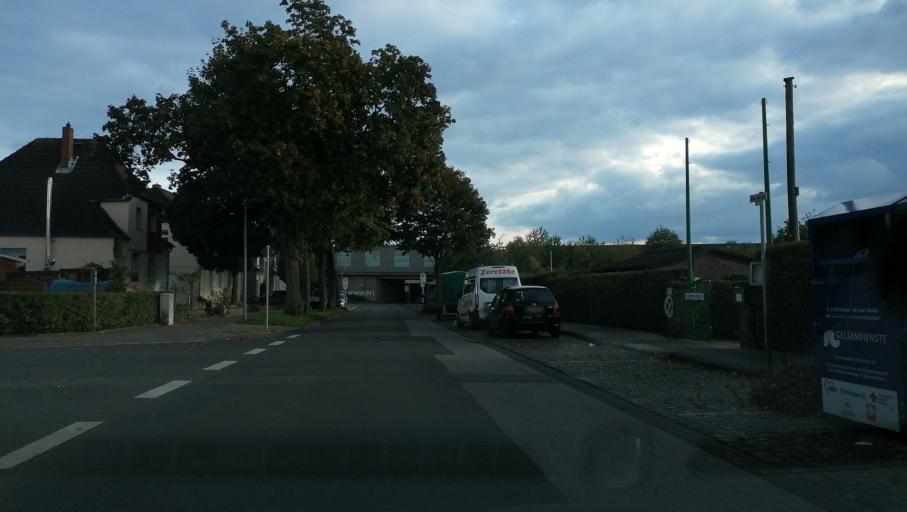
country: DE
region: North Rhine-Westphalia
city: Herten
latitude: 51.5713
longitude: 7.1130
